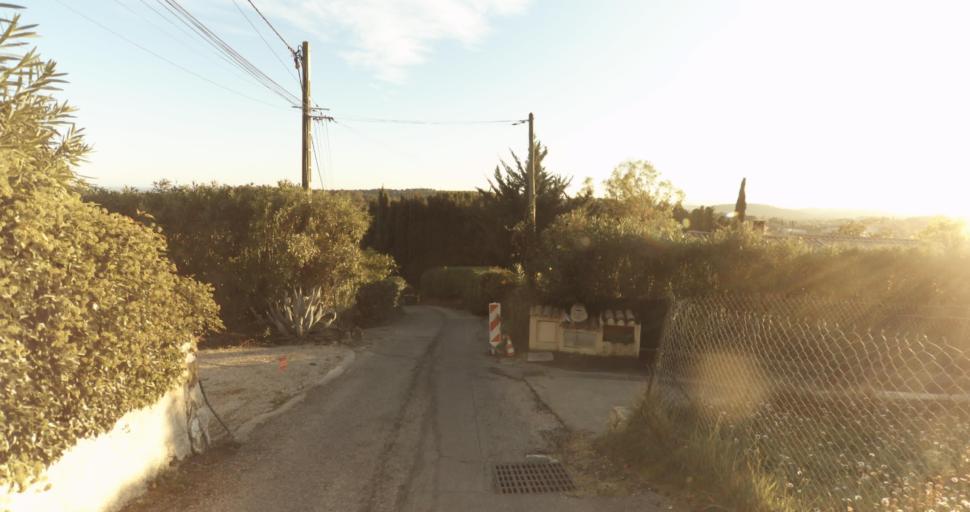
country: FR
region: Provence-Alpes-Cote d'Azur
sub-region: Departement des Alpes-Maritimes
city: Vence
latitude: 43.7267
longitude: 7.0927
